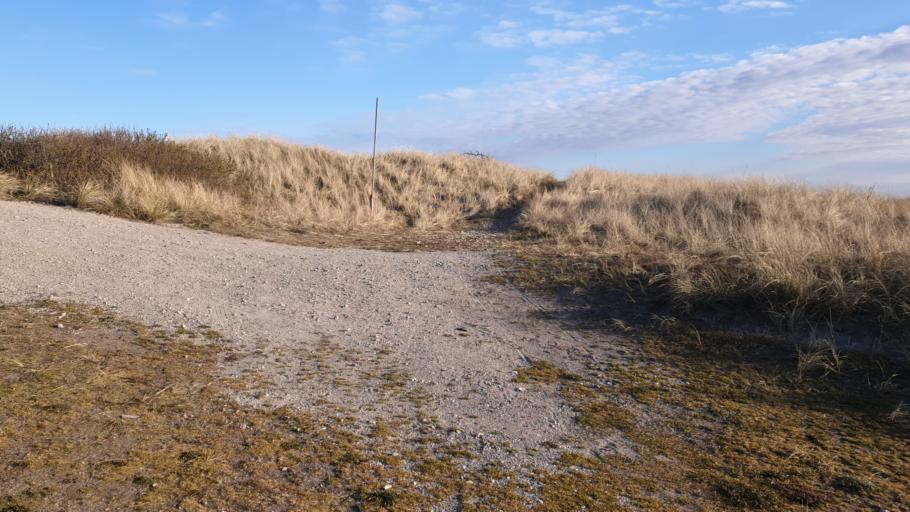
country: DK
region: North Denmark
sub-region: Hjorring Kommune
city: Hjorring
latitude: 57.4862
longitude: 9.8138
